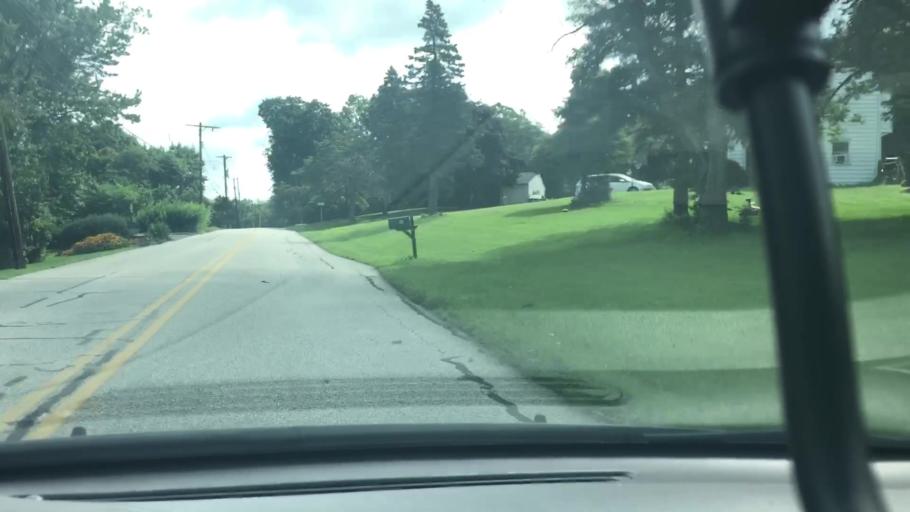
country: US
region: Pennsylvania
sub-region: Chester County
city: Kenilworth
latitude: 40.1804
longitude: -75.6535
